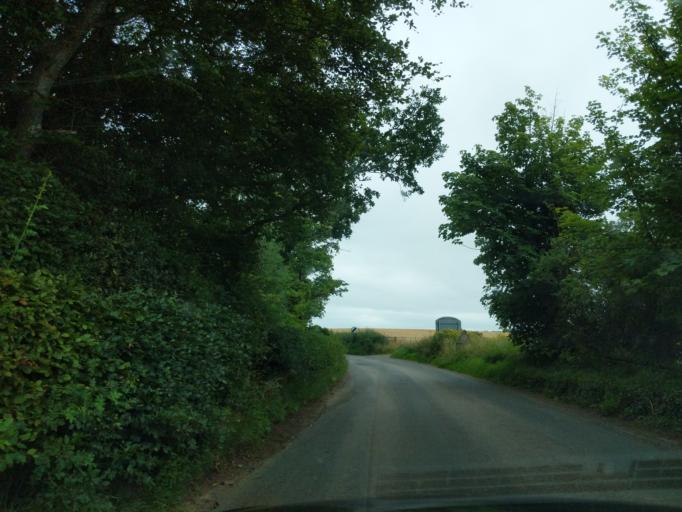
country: GB
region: Scotland
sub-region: East Lothian
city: Pencaitland
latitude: 55.9055
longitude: -2.8913
